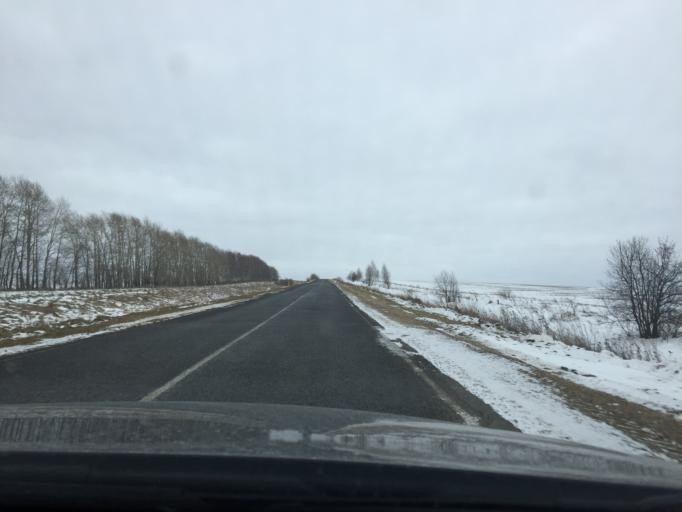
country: RU
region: Tula
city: Shchekino
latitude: 53.8292
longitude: 37.5123
